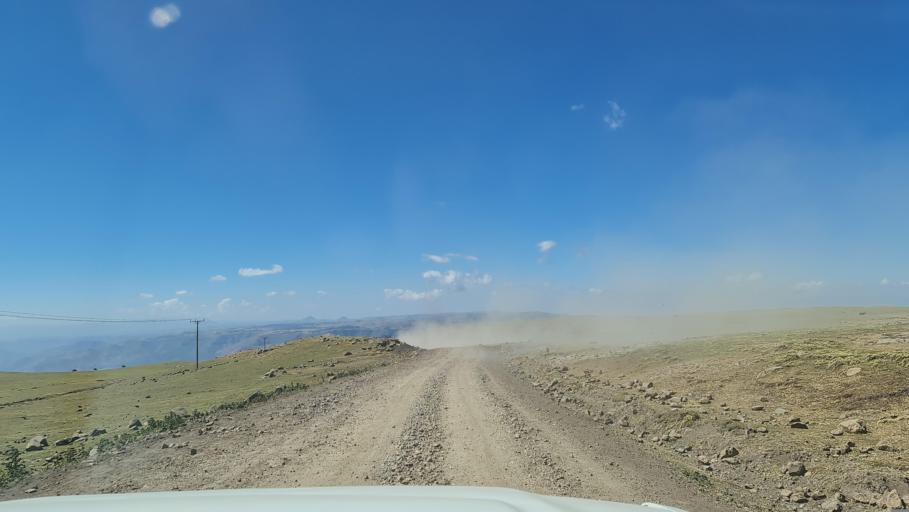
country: ET
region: Amhara
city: Debark'
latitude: 13.2391
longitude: 38.1163
